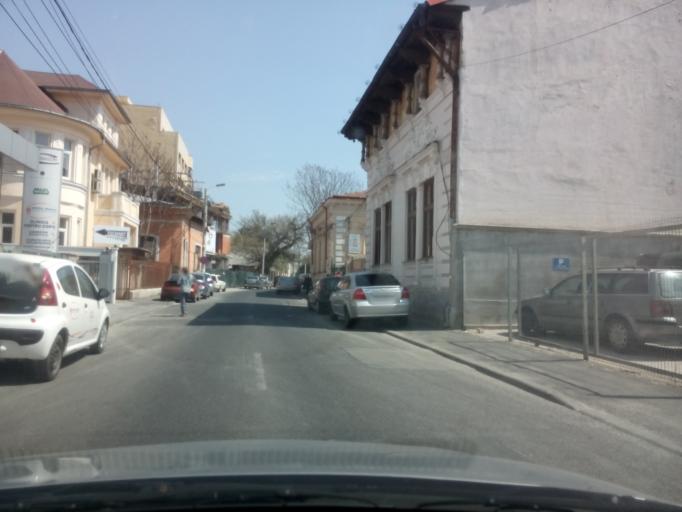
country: RO
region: Bucuresti
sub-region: Municipiul Bucuresti
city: Bucharest
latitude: 44.4305
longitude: 26.1153
